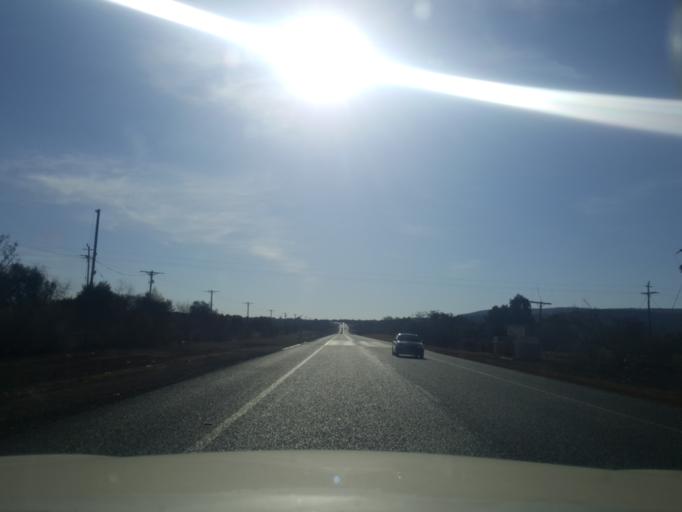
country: ZA
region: North-West
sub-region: Ngaka Modiri Molema District Municipality
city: Zeerust
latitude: -25.5481
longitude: 26.0533
